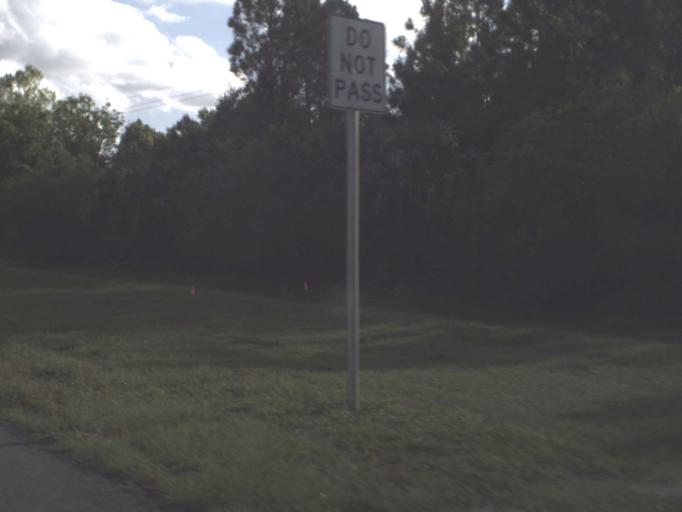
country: US
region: Florida
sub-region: Flagler County
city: Bunnell
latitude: 29.3448
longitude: -81.3110
